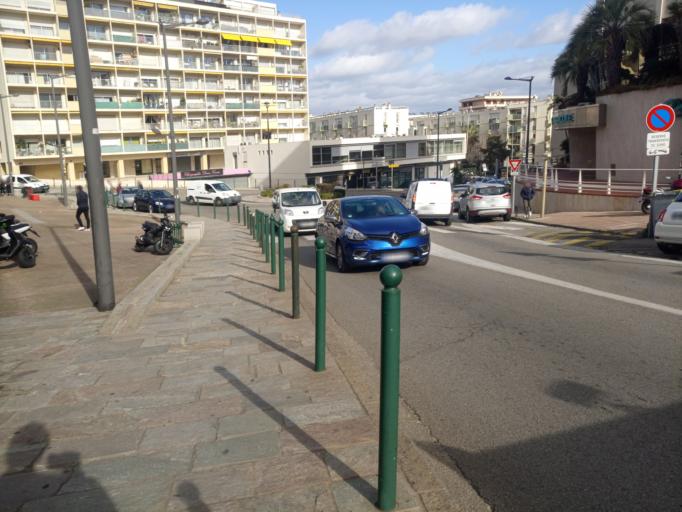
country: FR
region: Corsica
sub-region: Departement de la Corse-du-Sud
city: Ajaccio
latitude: 41.9264
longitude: 8.7345
